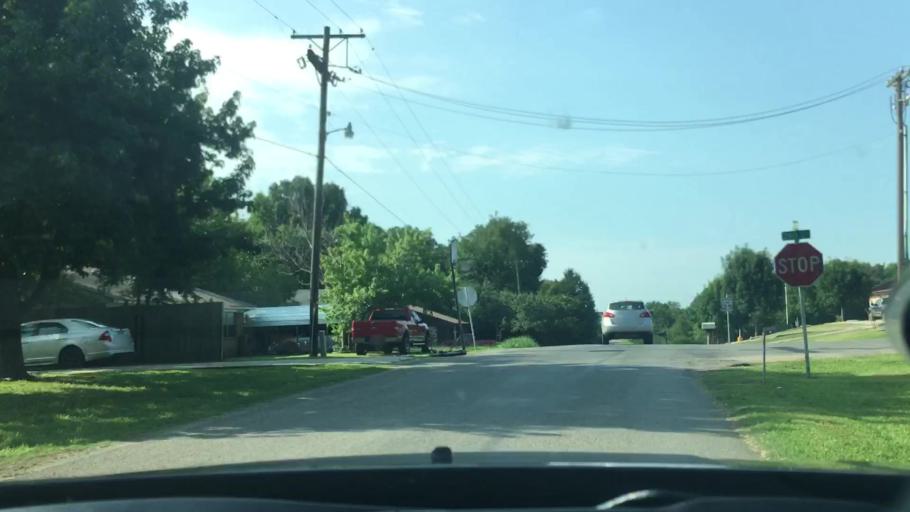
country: US
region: Oklahoma
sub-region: Johnston County
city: Tishomingo
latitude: 34.2236
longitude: -96.6711
